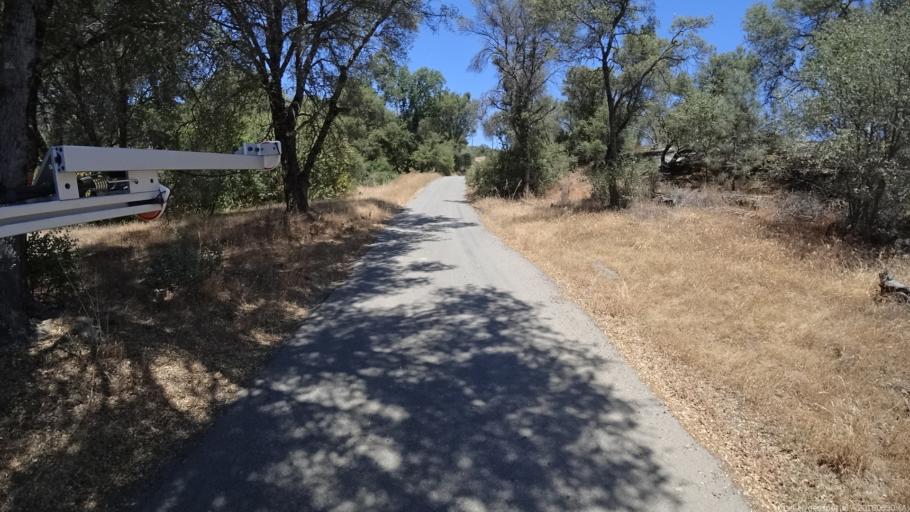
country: US
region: California
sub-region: Fresno County
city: Auberry
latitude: 37.2141
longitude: -119.4881
